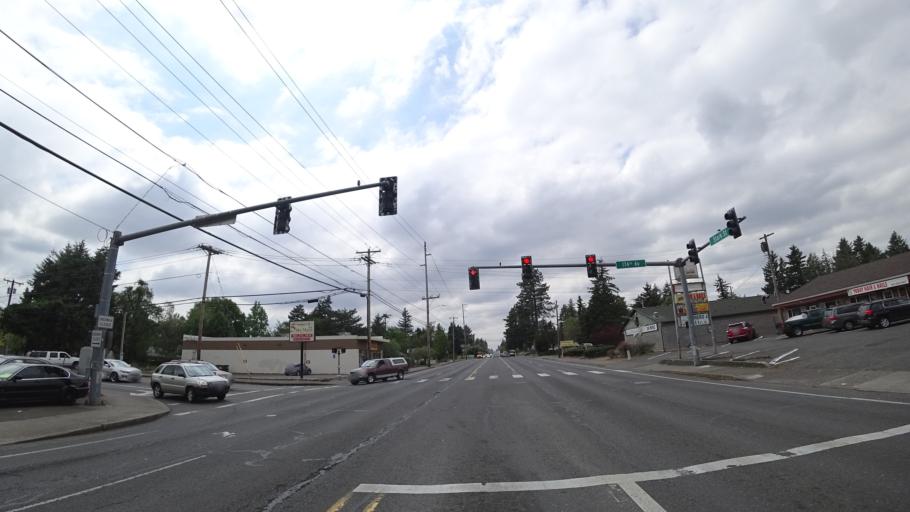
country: US
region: Oregon
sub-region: Multnomah County
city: Fairview
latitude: 45.5192
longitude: -122.4842
